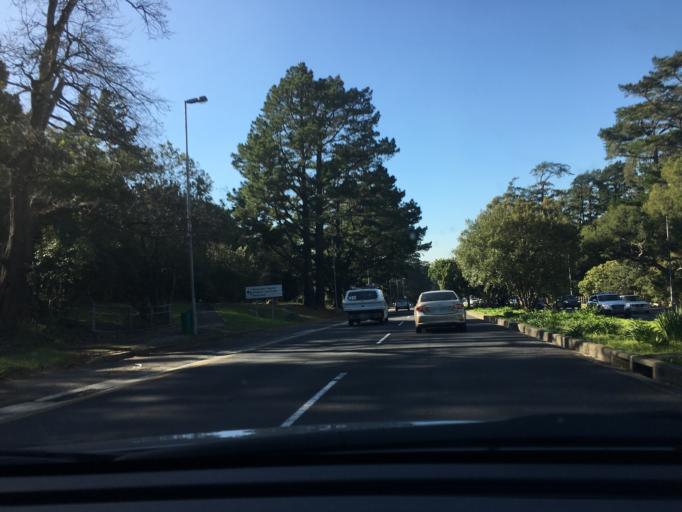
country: ZA
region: Western Cape
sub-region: City of Cape Town
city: Newlands
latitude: -33.9726
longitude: 18.4489
